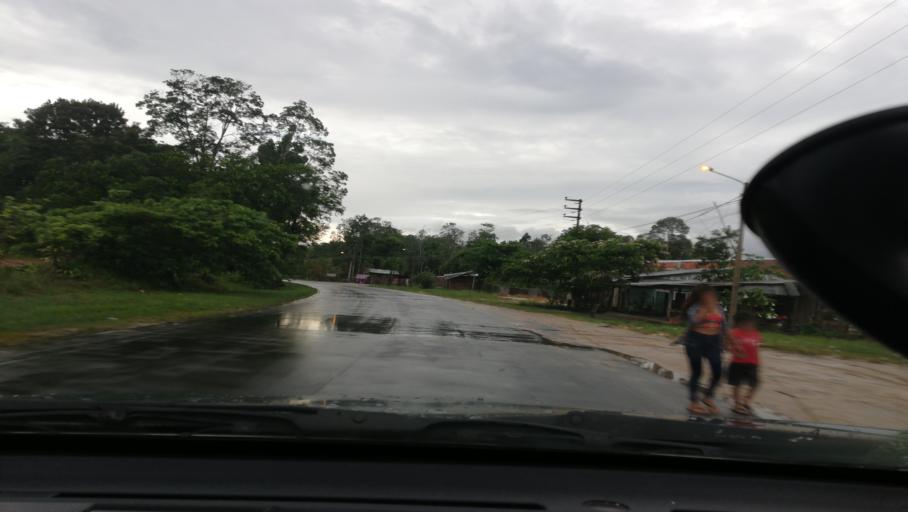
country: PE
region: Loreto
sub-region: Provincia de Maynas
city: Iquitos
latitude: -3.8906
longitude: -73.3509
